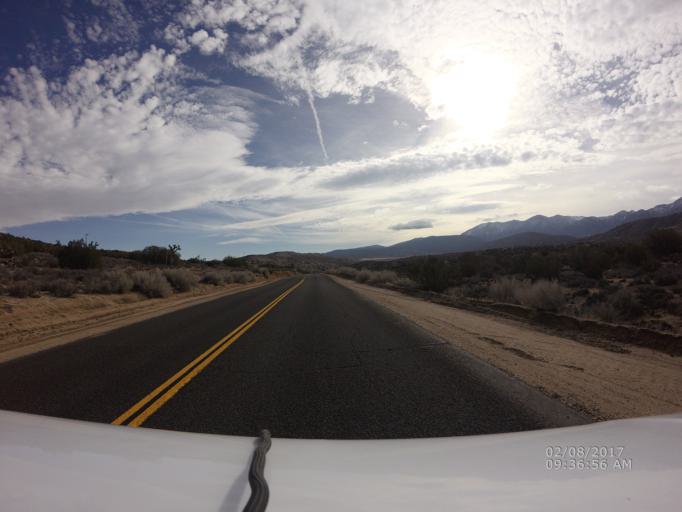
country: US
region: California
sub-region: Los Angeles County
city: Littlerock
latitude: 34.4622
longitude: -117.8756
